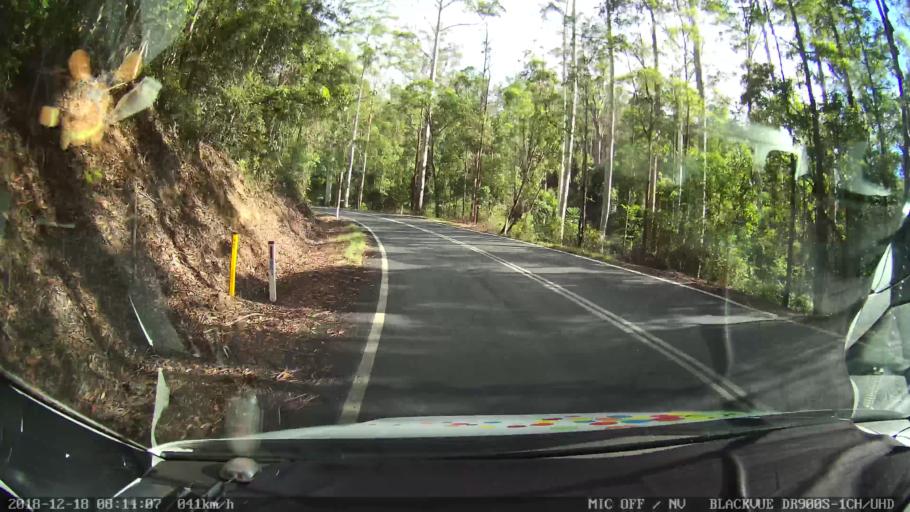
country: AU
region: New South Wales
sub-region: Kyogle
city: Kyogle
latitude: -28.3370
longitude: 152.6803
